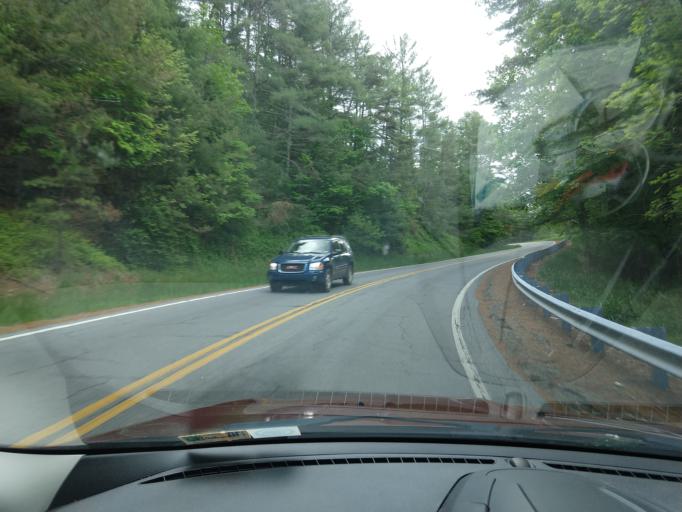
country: US
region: Virginia
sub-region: City of Galax
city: Galax
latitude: 36.7711
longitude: -80.9831
